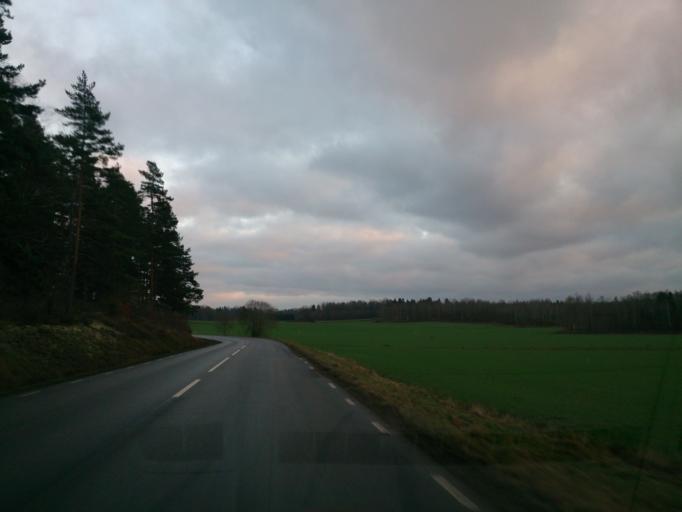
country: SE
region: OEstergoetland
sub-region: Norrkopings Kommun
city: Kimstad
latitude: 58.3970
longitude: 15.9551
